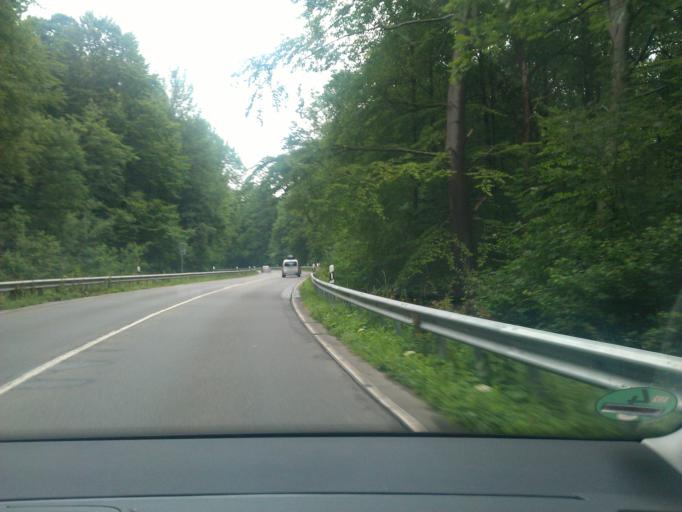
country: DE
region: North Rhine-Westphalia
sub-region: Regierungsbezirk Koln
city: Aachen
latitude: 50.7418
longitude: 6.1079
